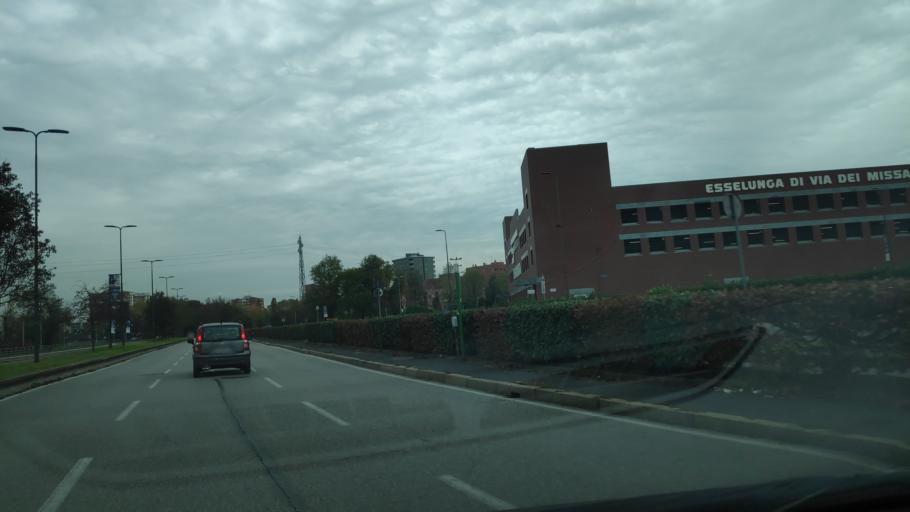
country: IT
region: Lombardy
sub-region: Citta metropolitana di Milano
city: Rozzano
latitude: 45.4202
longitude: 9.1762
